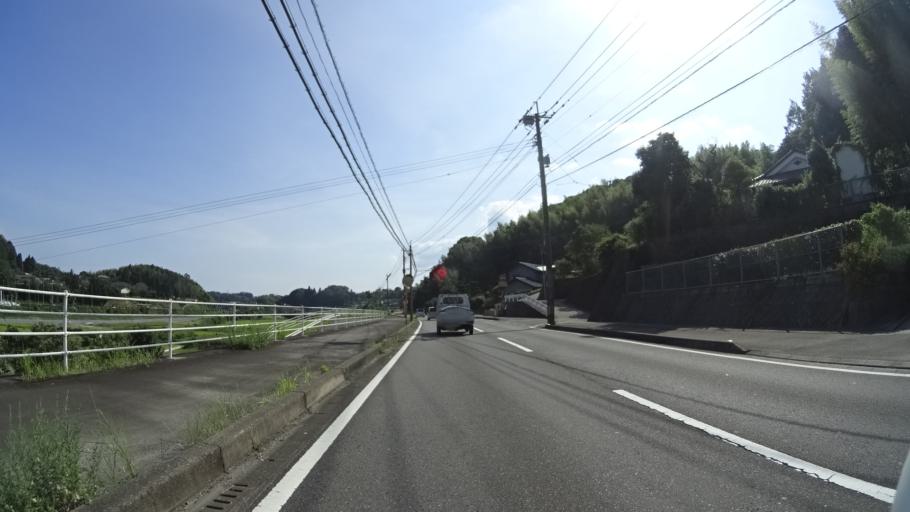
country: JP
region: Kagoshima
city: Kagoshima-shi
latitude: 31.6602
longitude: 130.5511
